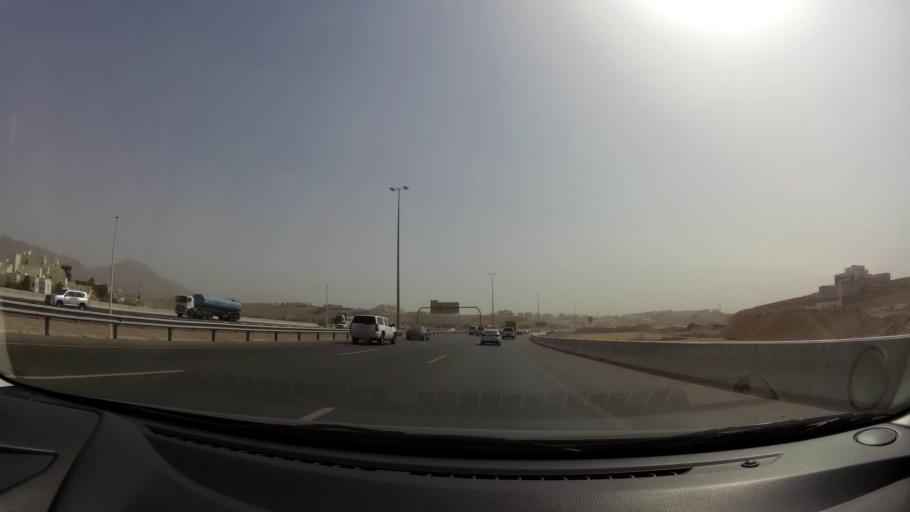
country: OM
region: Muhafazat Masqat
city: Bawshar
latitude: 23.5649
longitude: 58.3941
